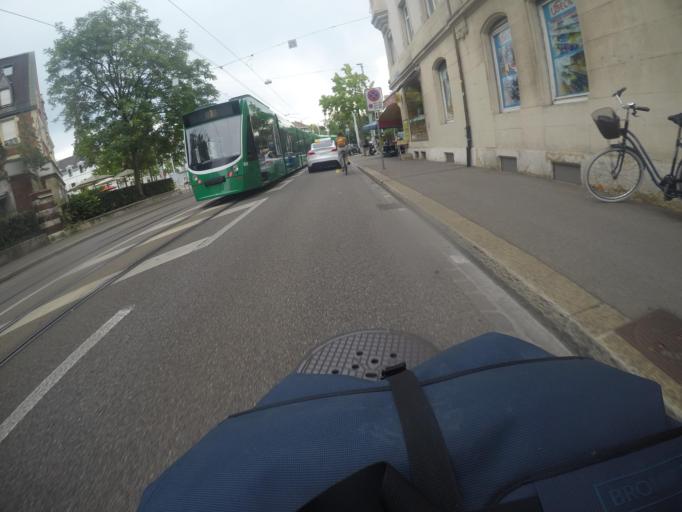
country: CH
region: Basel-City
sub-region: Basel-Stadt
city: Basel
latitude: 47.5599
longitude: 7.5980
